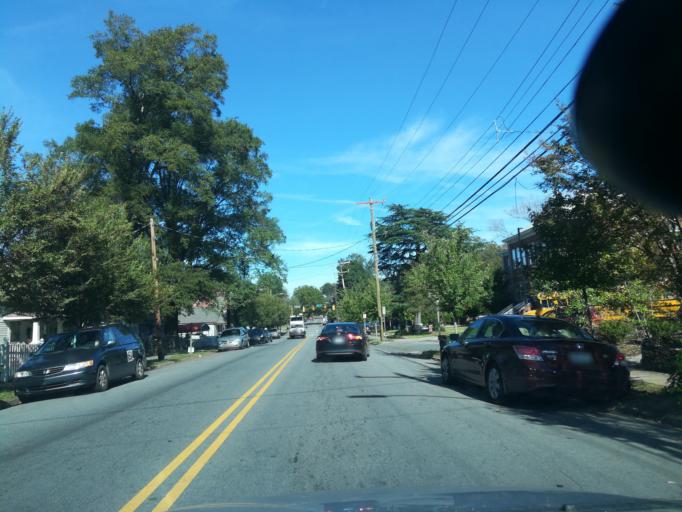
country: US
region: North Carolina
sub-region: Durham County
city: Durham
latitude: 35.9846
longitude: -78.8778
